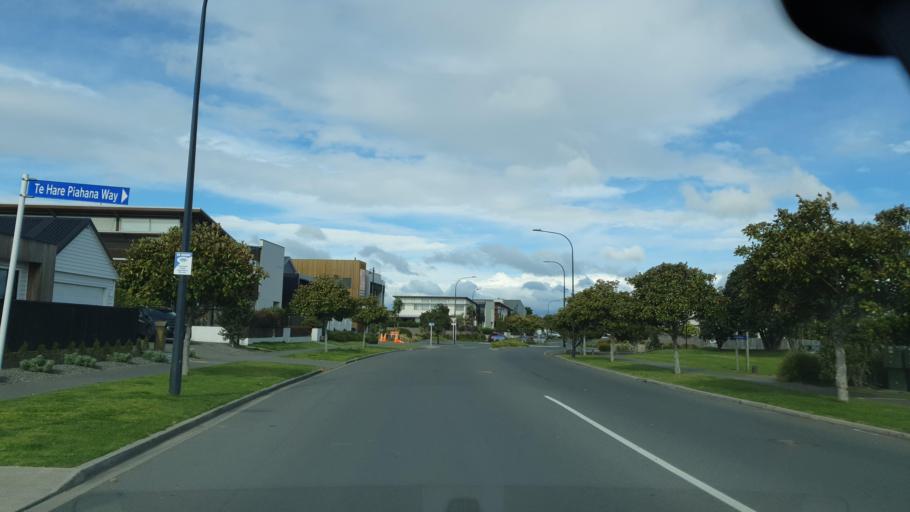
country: NZ
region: Bay of Plenty
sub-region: Tauranga City
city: Tauranga
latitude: -37.6874
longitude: 176.2460
